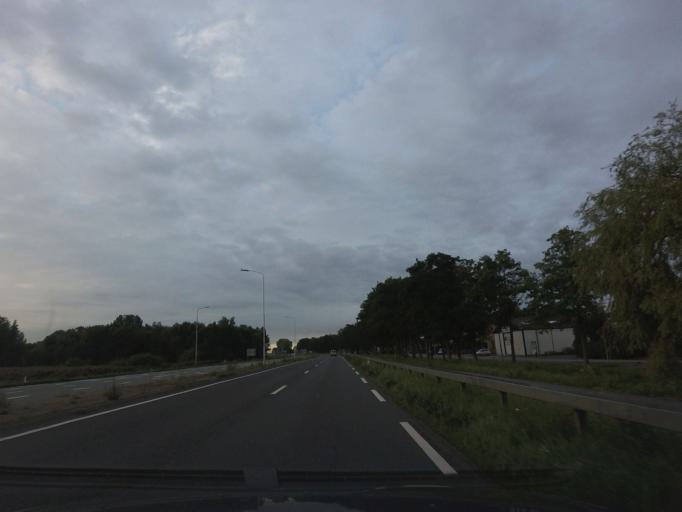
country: NL
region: North Holland
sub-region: Gemeente Zaanstad
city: Zaanstad
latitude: 52.5039
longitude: 4.7780
